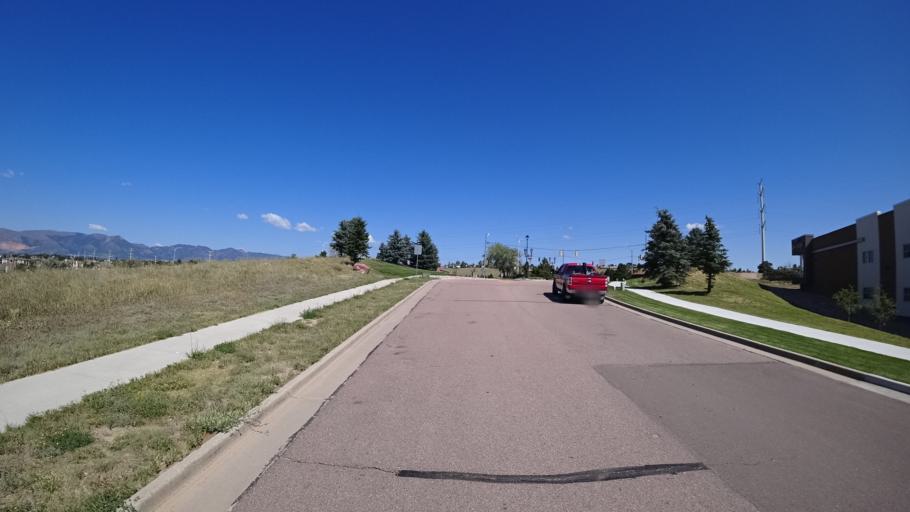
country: US
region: Colorado
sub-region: El Paso County
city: Black Forest
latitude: 38.9393
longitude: -104.7480
